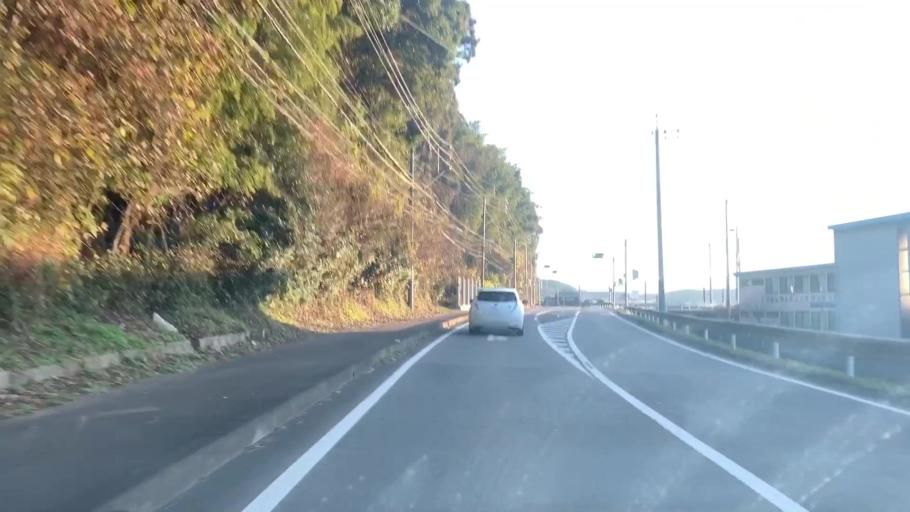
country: JP
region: Saga Prefecture
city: Imaricho-ko
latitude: 33.2879
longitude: 129.9708
